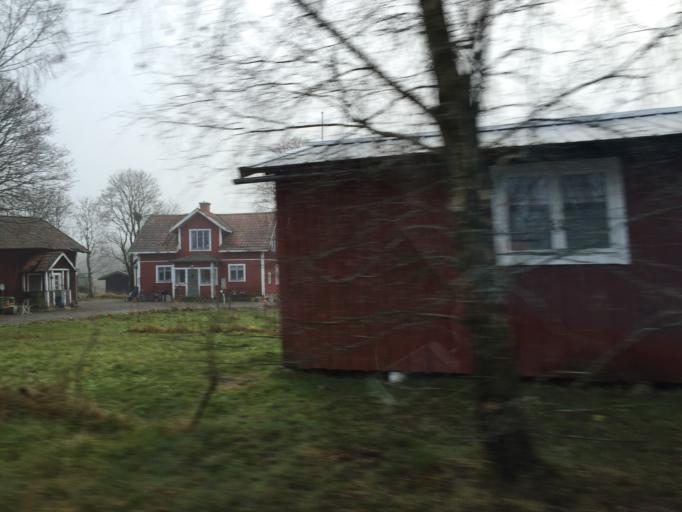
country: SE
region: Stockholm
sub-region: Nynashamns Kommun
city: Osmo
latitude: 59.0507
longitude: 17.8871
